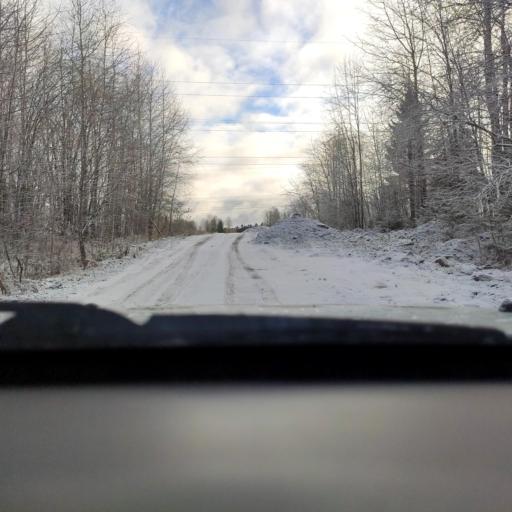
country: RU
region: Perm
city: Ferma
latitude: 58.0093
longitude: 56.4038
